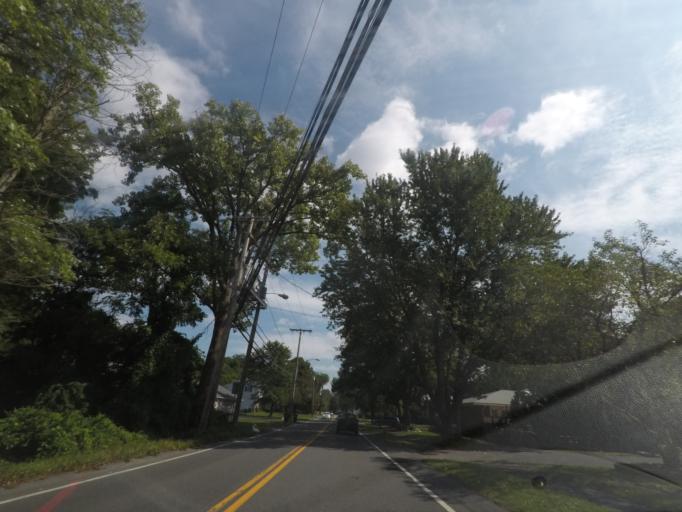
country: US
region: New York
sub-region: Albany County
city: Delmar
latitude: 42.6246
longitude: -73.8508
